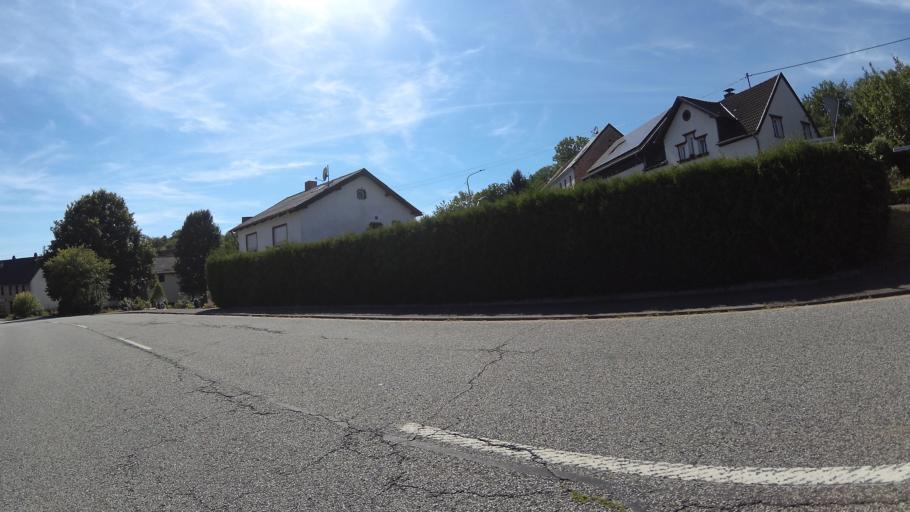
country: DE
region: Rheinland-Pfalz
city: Hornbach
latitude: 49.1706
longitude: 7.3112
